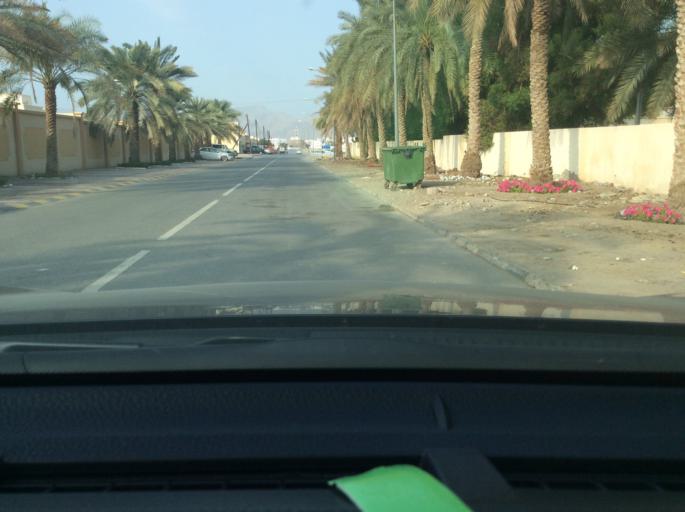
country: OM
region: Muhafazat Masqat
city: Bawshar
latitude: 23.4882
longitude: 58.5035
